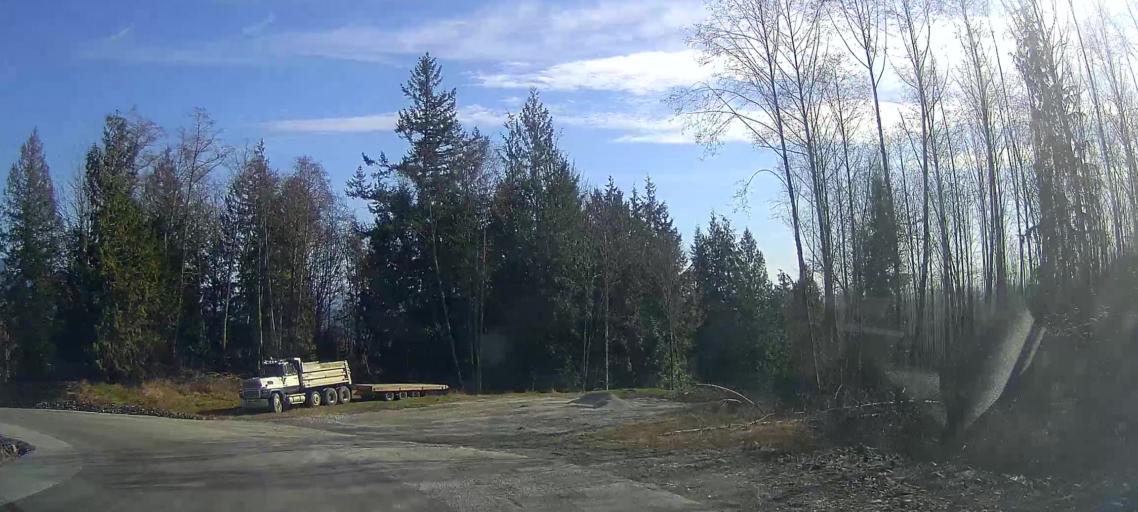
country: US
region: Washington
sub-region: Whatcom County
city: Sudden Valley
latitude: 48.5964
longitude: -122.3848
